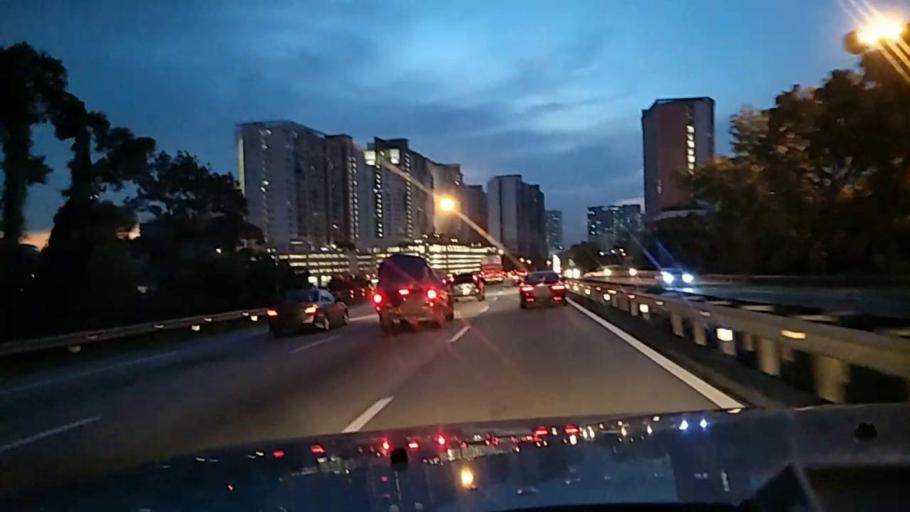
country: MY
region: Selangor
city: Shah Alam
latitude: 3.0650
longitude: 101.5568
